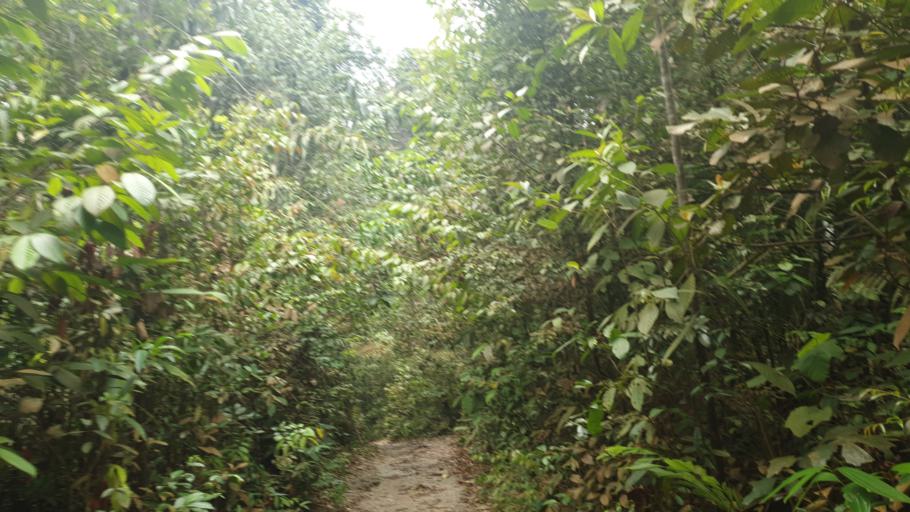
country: SG
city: Singapore
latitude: 1.3557
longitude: 103.8148
